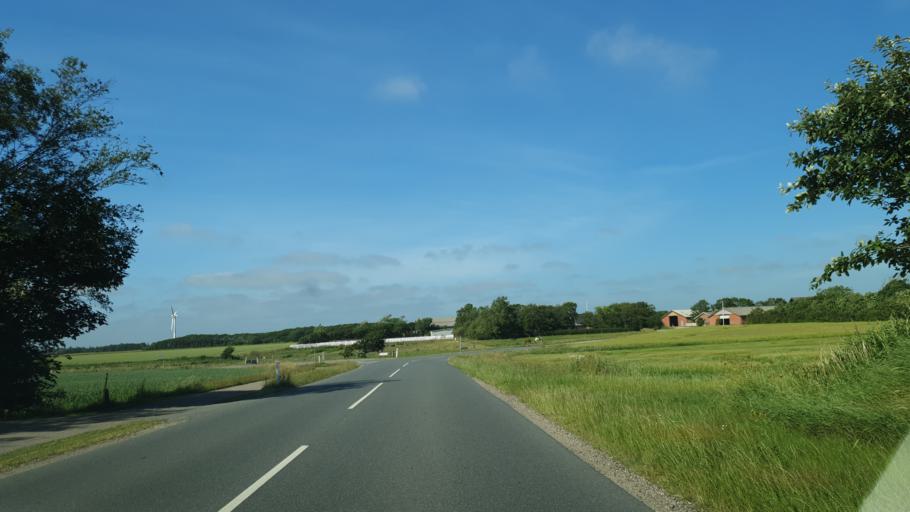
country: DK
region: Central Jutland
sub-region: Ringkobing-Skjern Kommune
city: Ringkobing
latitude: 56.0584
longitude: 8.3136
